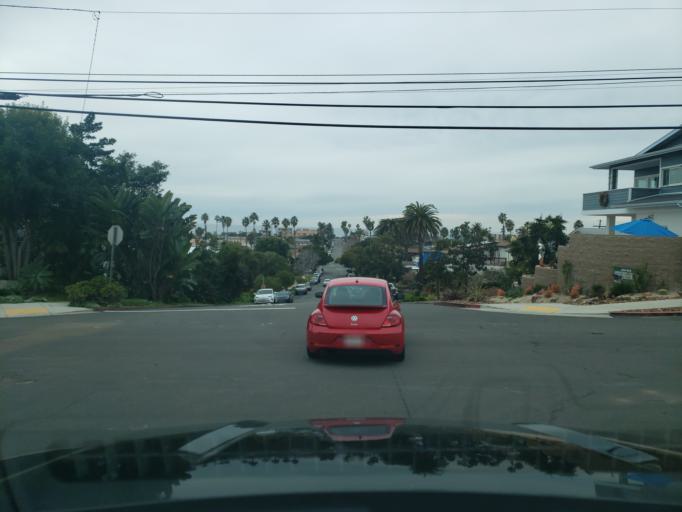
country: US
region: California
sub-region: San Diego County
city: Coronado
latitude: 32.7386
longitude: -117.2501
